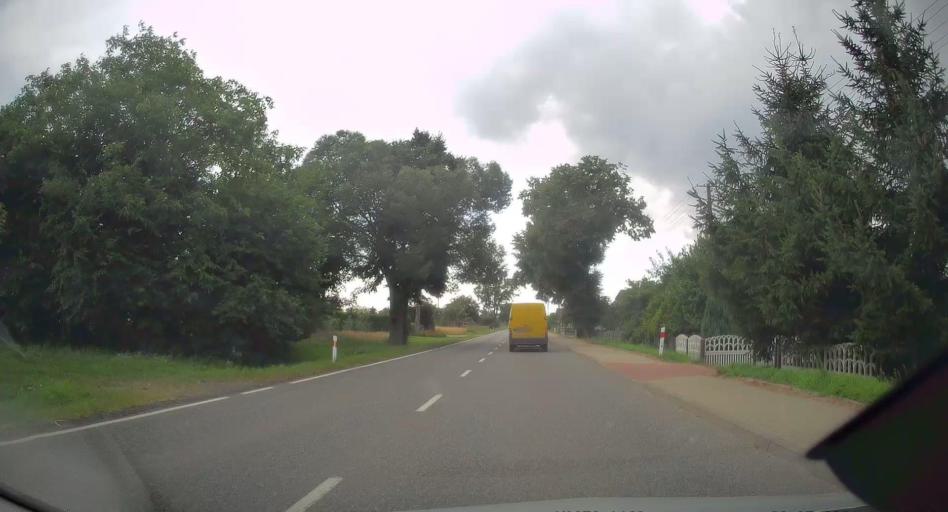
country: PL
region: Lodz Voivodeship
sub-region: Powiat skierniewicki
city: Gluchow
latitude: 51.7748
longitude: 20.1271
